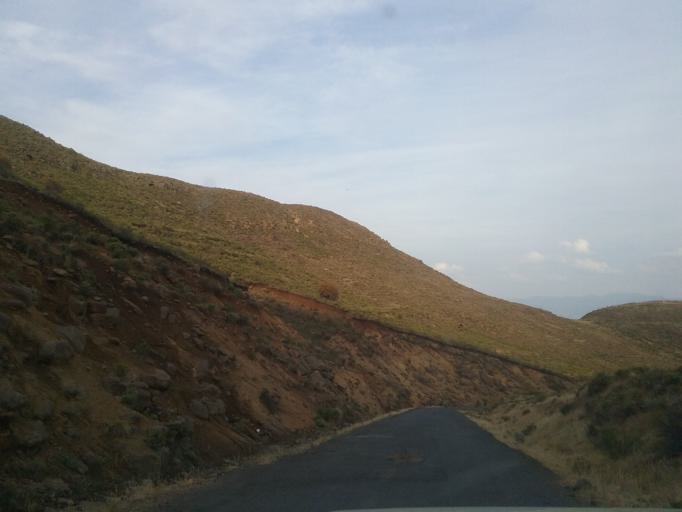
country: LS
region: Quthing
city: Quthing
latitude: -30.1923
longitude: 27.9702
